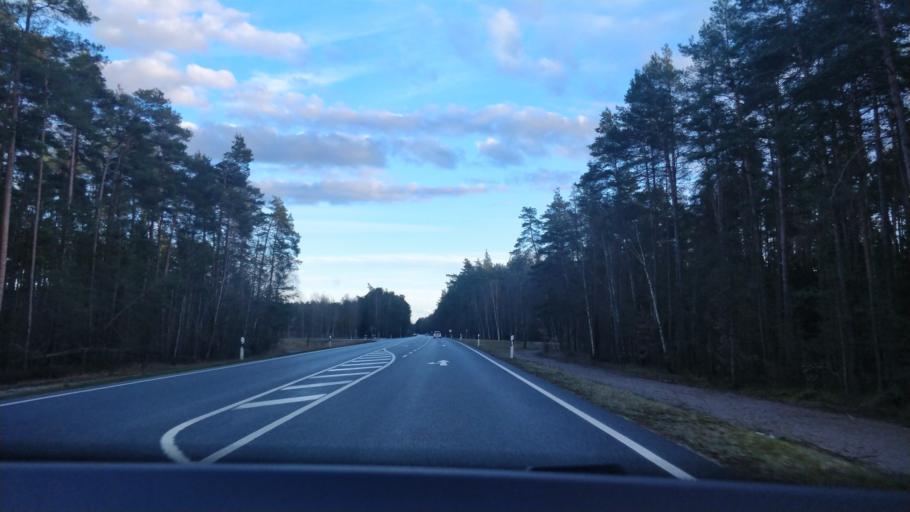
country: DE
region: Bavaria
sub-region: Upper Palatinate
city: Pressath
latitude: 49.7393
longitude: 11.9487
